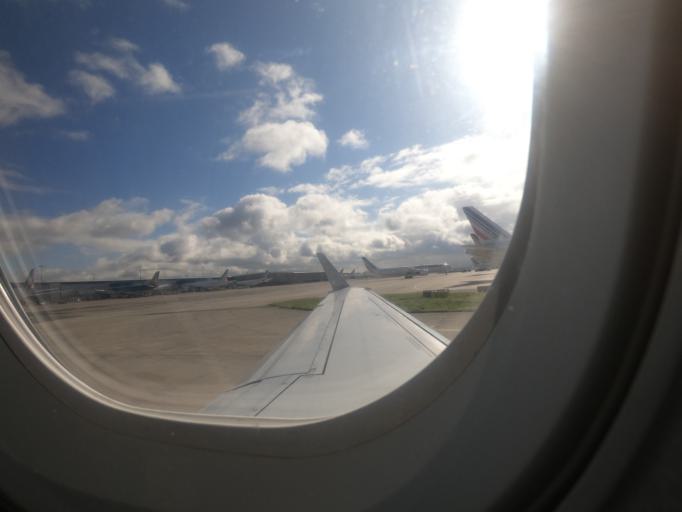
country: FR
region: Ile-de-France
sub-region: Departement de Seine-et-Marne
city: Mitry-Mory
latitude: 49.0084
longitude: 2.5860
